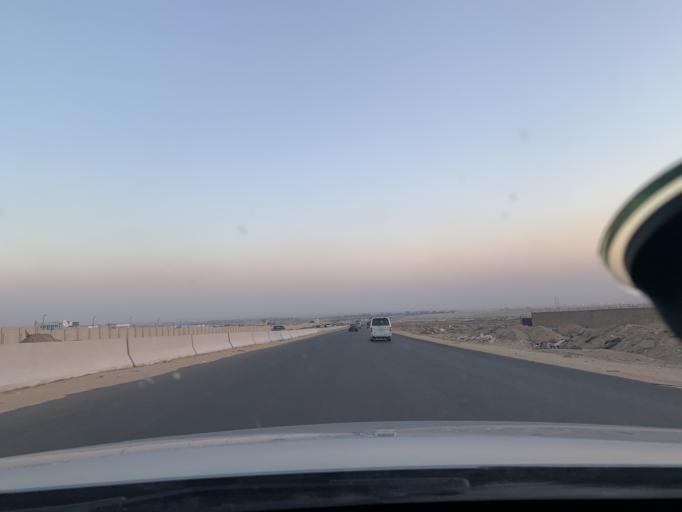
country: EG
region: Muhafazat al Qalyubiyah
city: Al Khankah
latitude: 30.2222
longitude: 31.4262
